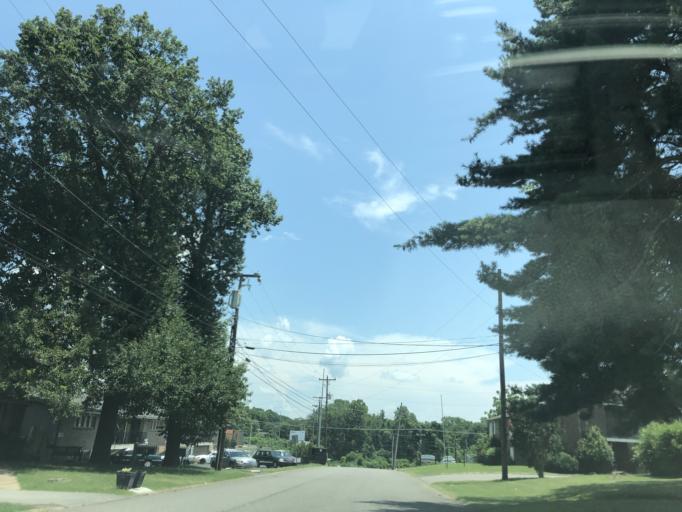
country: US
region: Tennessee
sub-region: Davidson County
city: Lakewood
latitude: 36.1928
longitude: -86.6267
